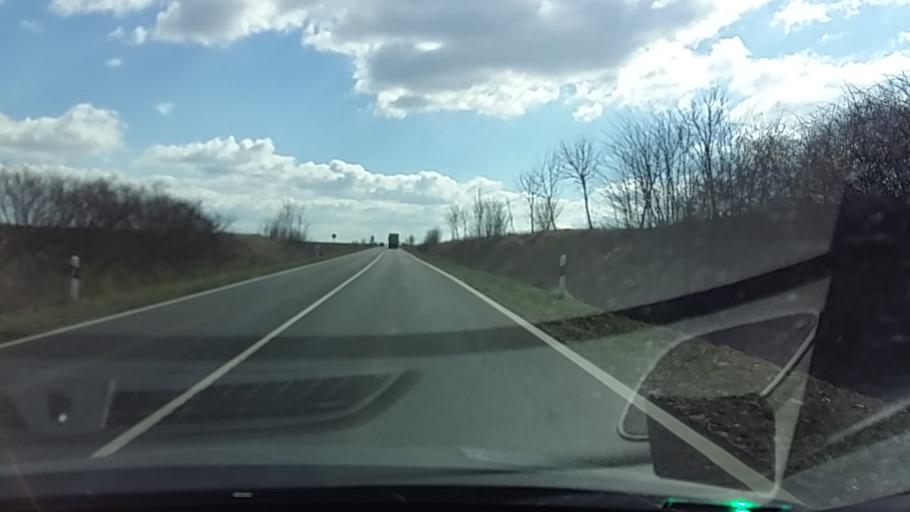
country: HU
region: Baranya
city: Kozarmisleny
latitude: 46.0420
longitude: 18.2718
